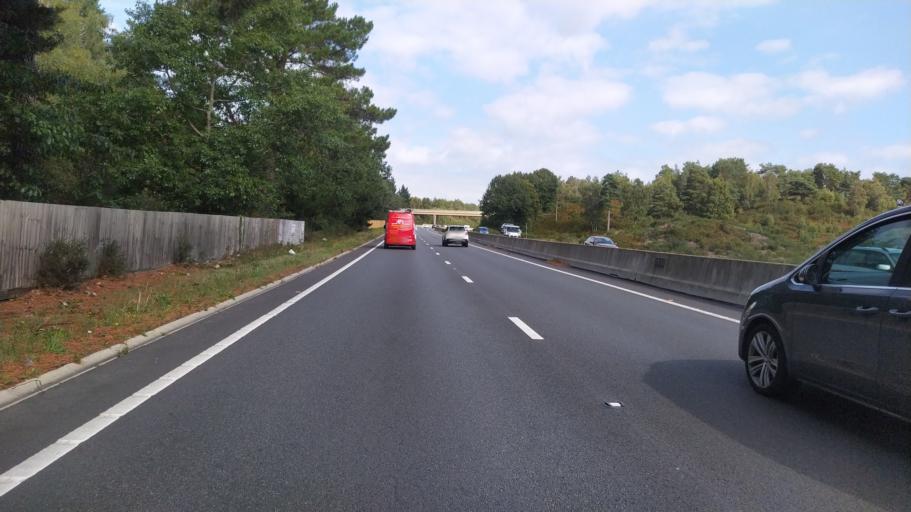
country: GB
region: England
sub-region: Hampshire
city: Ringwood
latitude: 50.8154
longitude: -1.8140
